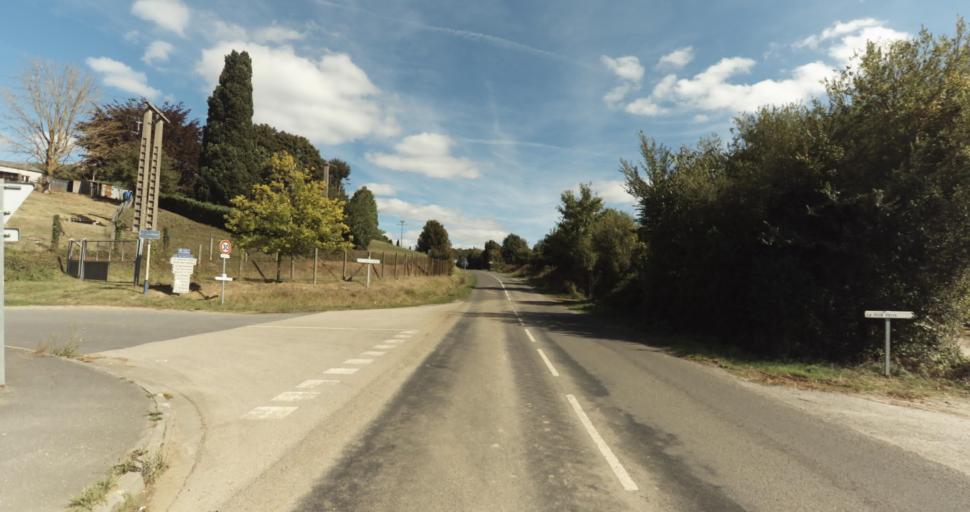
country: FR
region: Lower Normandy
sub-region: Departement de l'Orne
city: Vimoutiers
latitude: 48.9358
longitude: 0.2021
